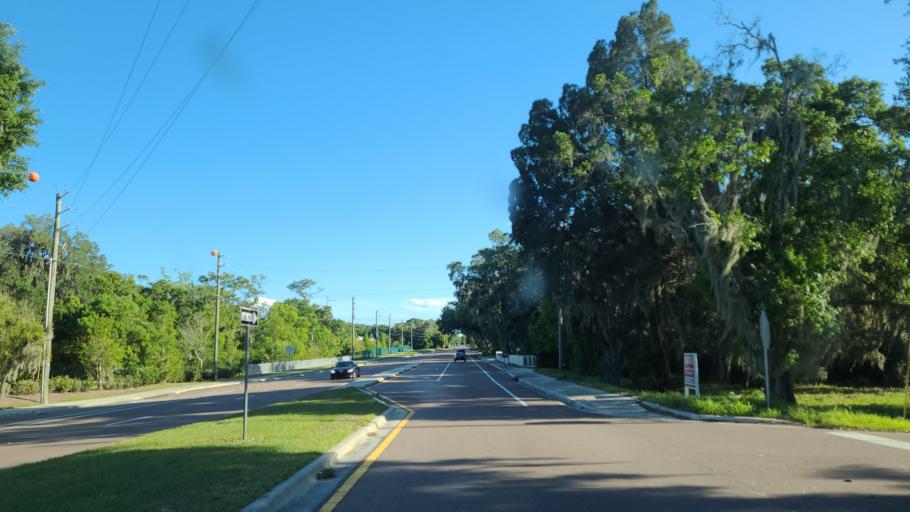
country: US
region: Florida
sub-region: Hillsborough County
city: Apollo Beach
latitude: 27.7876
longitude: -82.3474
